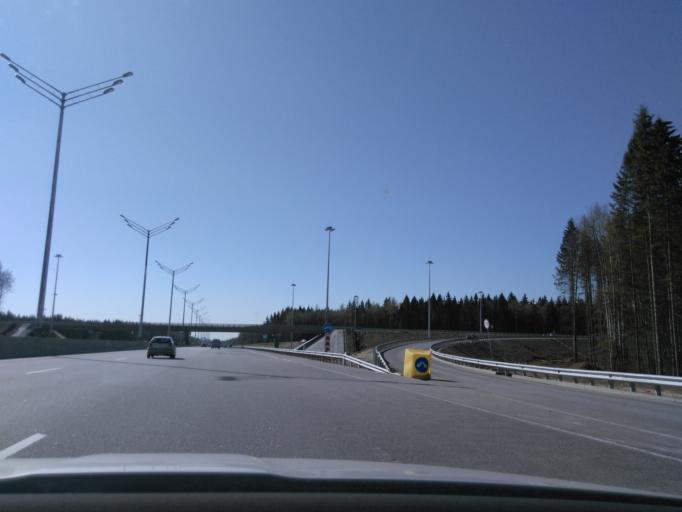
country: RU
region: Moskovskaya
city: Rzhavki
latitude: 56.0096
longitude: 37.2869
